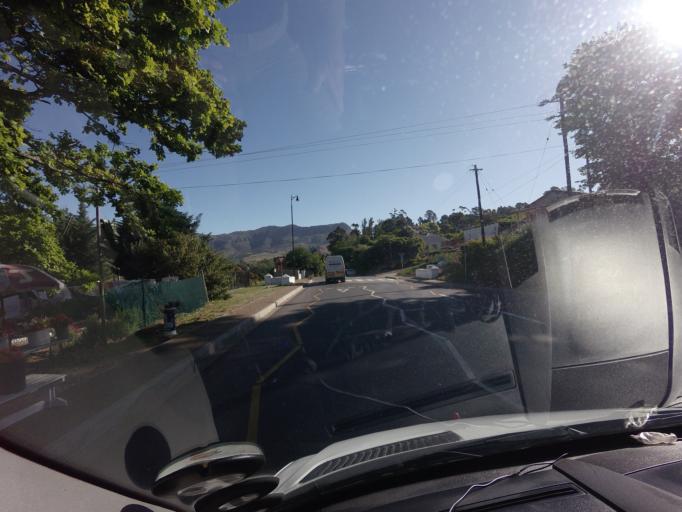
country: ZA
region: Western Cape
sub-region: Cape Winelands District Municipality
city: Stellenbosch
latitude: -33.9043
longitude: 18.9527
